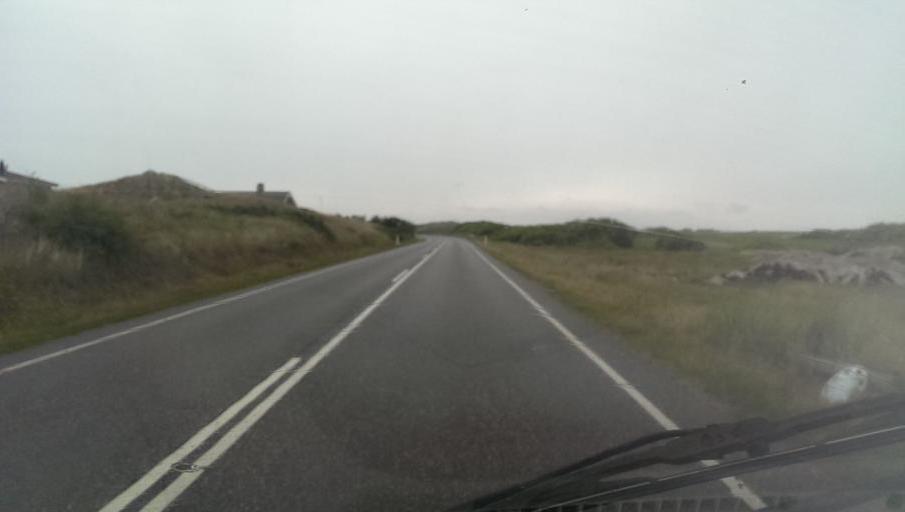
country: DK
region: Central Jutland
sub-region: Ringkobing-Skjern Kommune
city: Hvide Sande
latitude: 55.9075
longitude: 8.1666
